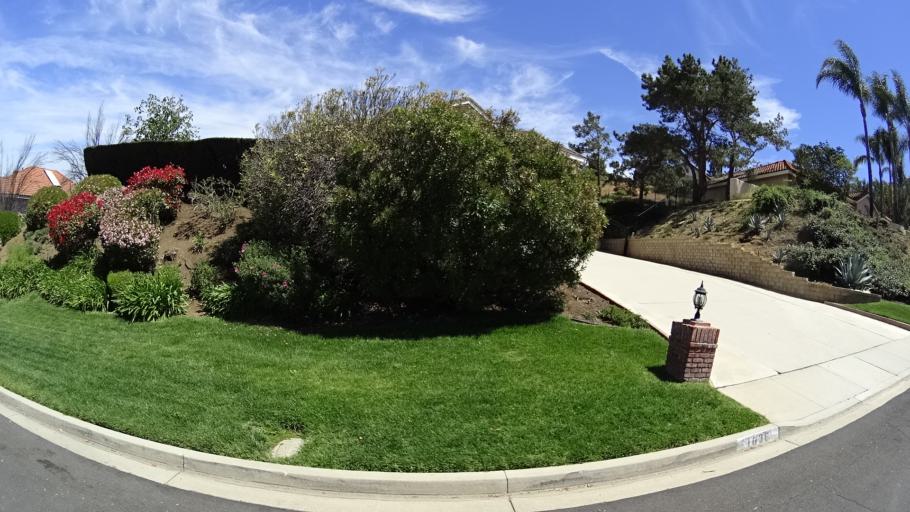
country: US
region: California
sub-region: Ventura County
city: Casa Conejo
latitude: 34.1583
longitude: -118.9455
